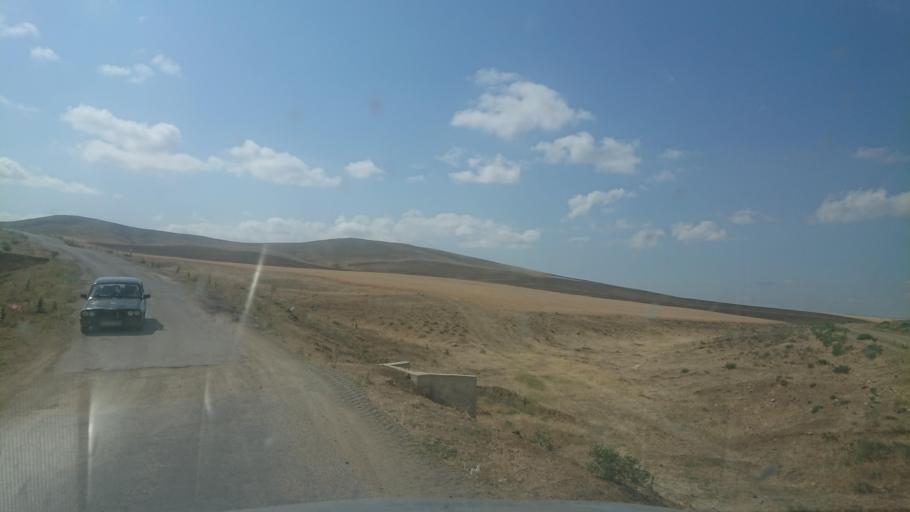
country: TR
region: Aksaray
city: Sariyahsi
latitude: 39.0080
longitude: 33.9500
